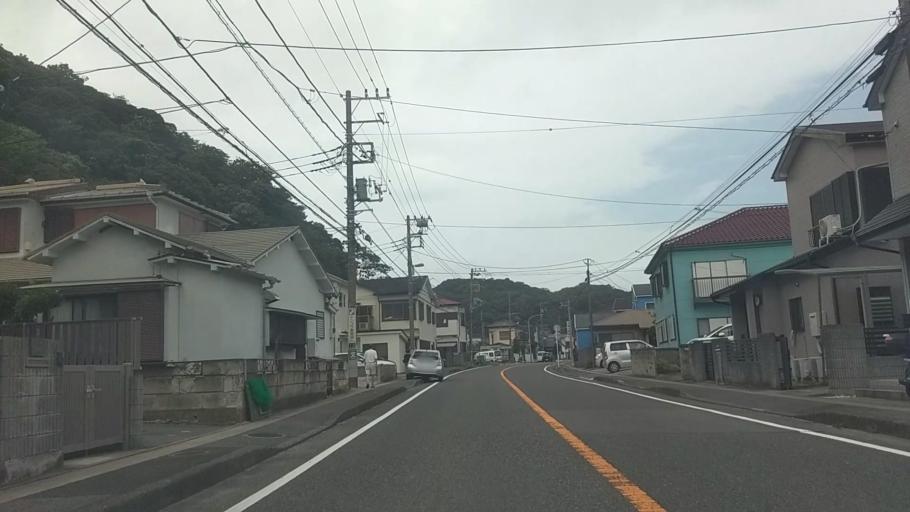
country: JP
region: Kanagawa
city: Yokosuka
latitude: 35.2504
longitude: 139.7367
